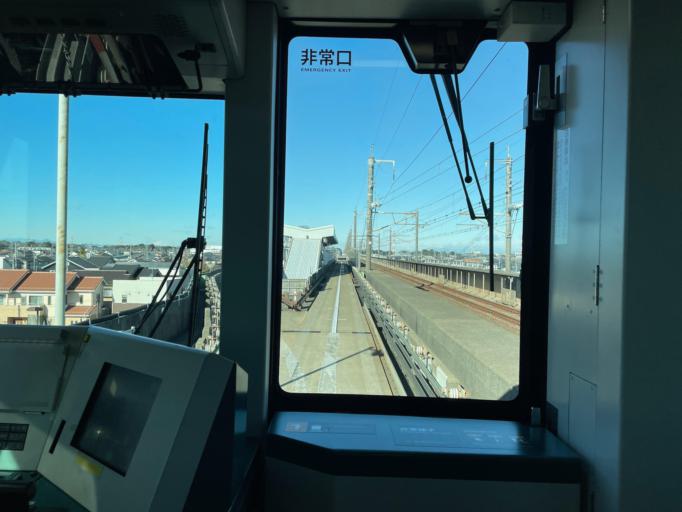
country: JP
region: Saitama
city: Ageoshimo
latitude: 36.0136
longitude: 139.6008
